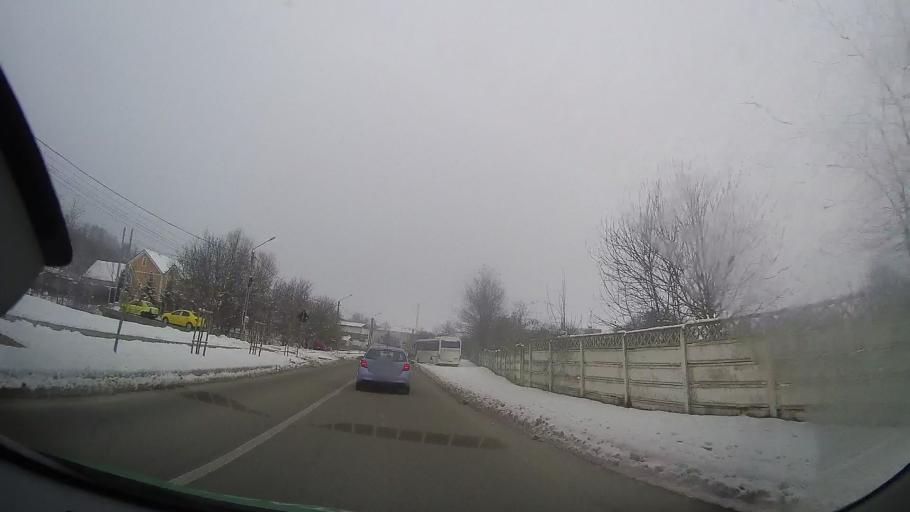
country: RO
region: Vaslui
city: Vaslui
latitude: 46.6444
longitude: 27.7201
